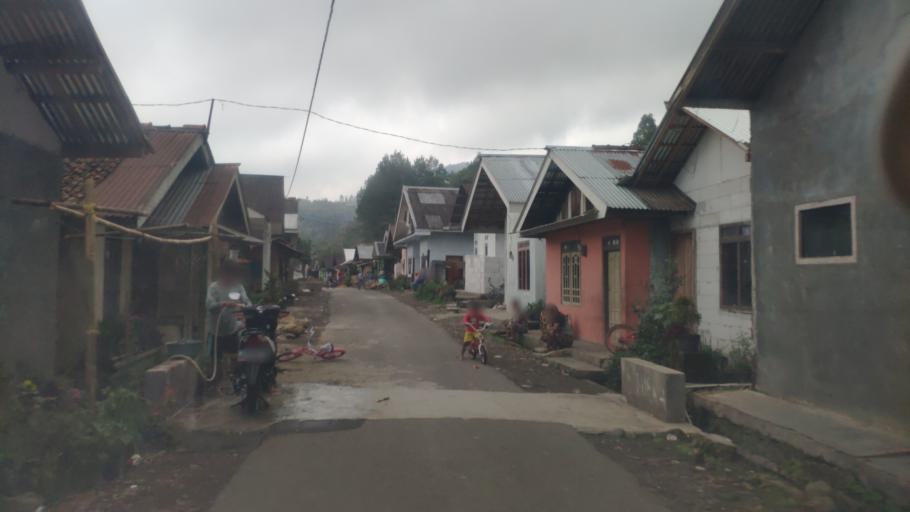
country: ID
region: Central Java
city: Wonosobo
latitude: -7.2299
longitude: 109.7277
